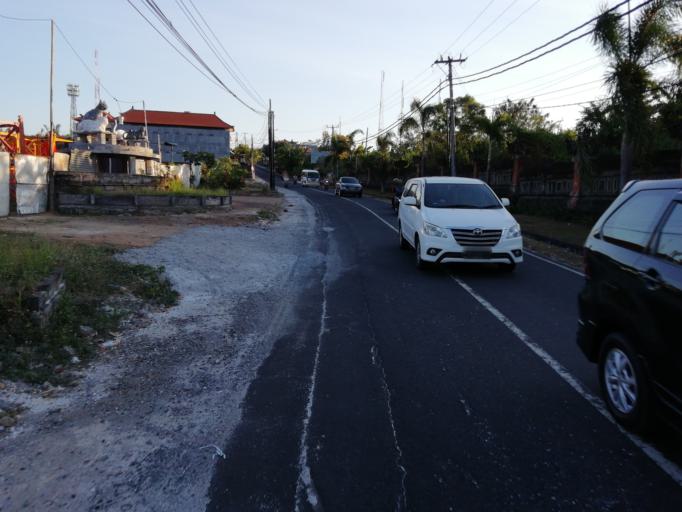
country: ID
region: Bali
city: Bualu
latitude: -8.8159
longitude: 115.1913
